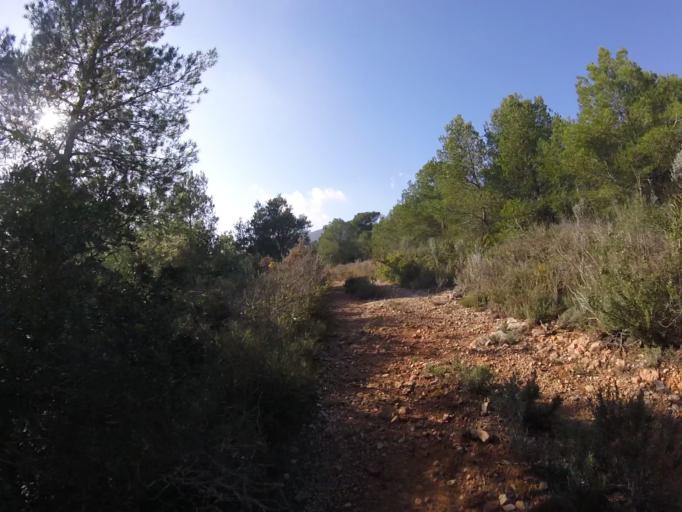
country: ES
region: Valencia
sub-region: Provincia de Castello
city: Alcoceber
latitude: 40.2917
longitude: 0.3192
